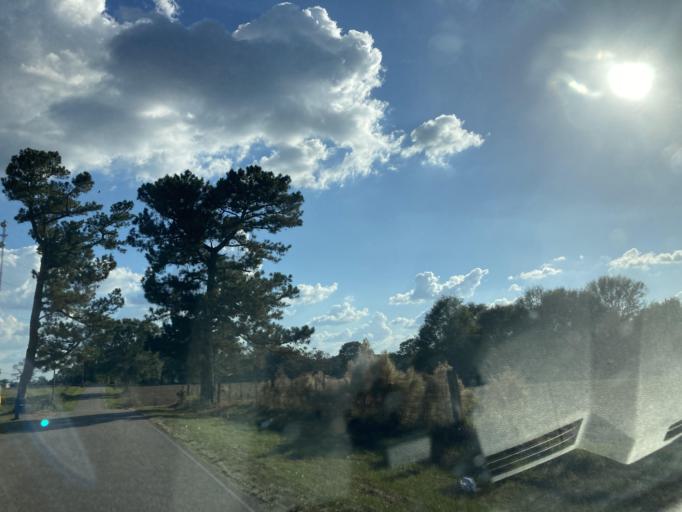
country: US
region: Mississippi
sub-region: Lamar County
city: Sumrall
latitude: 31.4325
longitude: -89.6378
